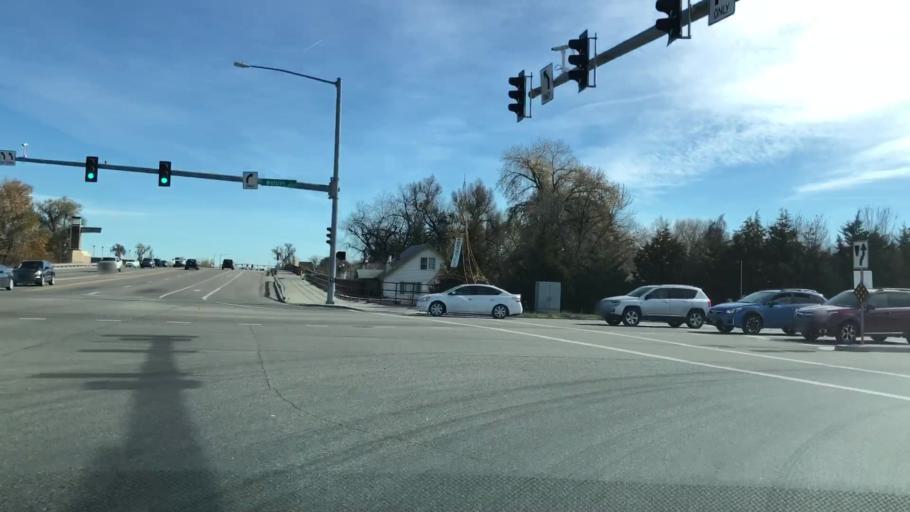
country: US
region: Colorado
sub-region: Weld County
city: Windsor
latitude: 40.5230
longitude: -104.9885
